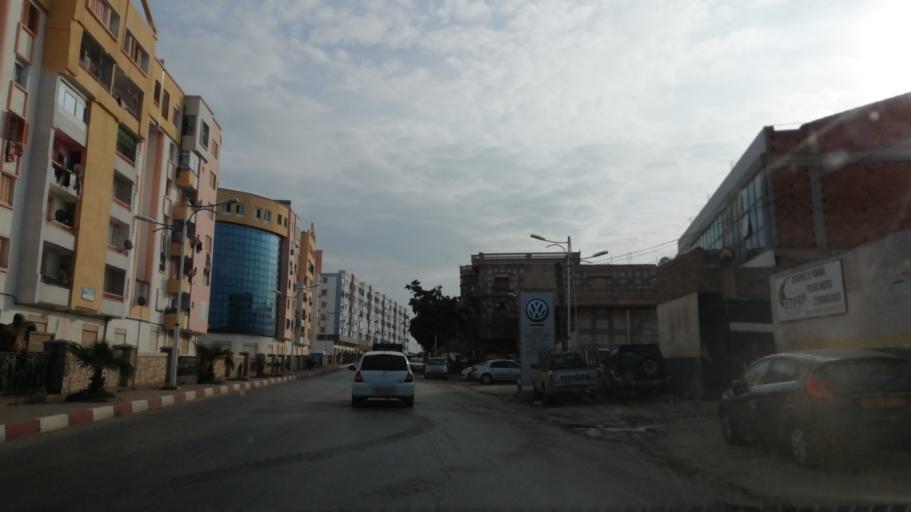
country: DZ
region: Mostaganem
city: Mostaganem
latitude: 35.8942
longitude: 0.0760
